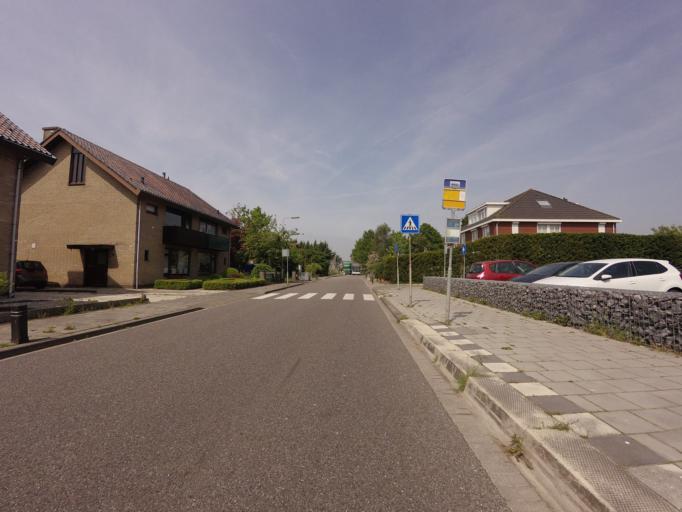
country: NL
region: South Holland
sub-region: Gemeente Hellevoetsluis
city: Nieuwenhoorn
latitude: 51.8299
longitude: 4.1896
